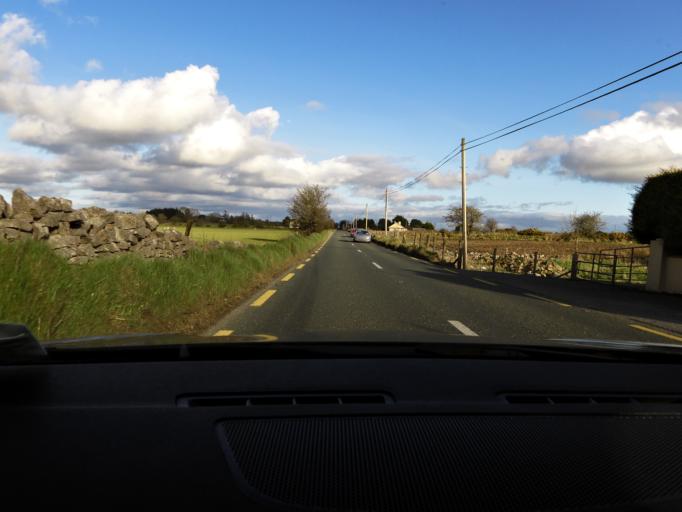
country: IE
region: Connaught
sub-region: Roscommon
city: Roscommon
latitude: 53.6505
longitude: -8.2372
